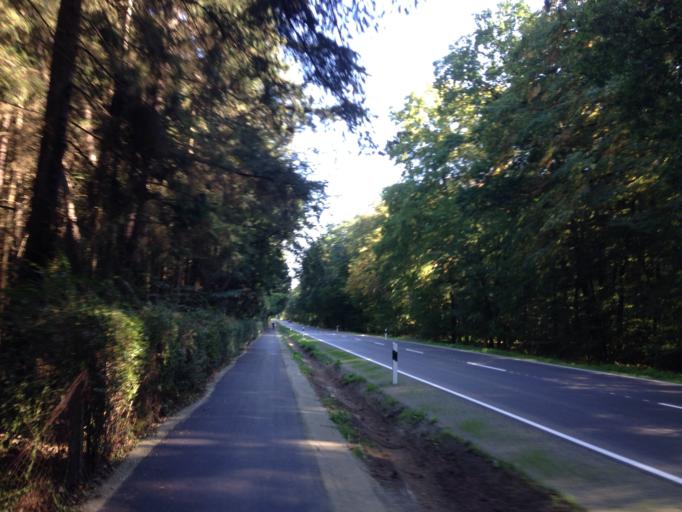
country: DE
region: Hesse
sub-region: Regierungsbezirk Giessen
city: Giessen
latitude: 50.5597
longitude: 8.7119
